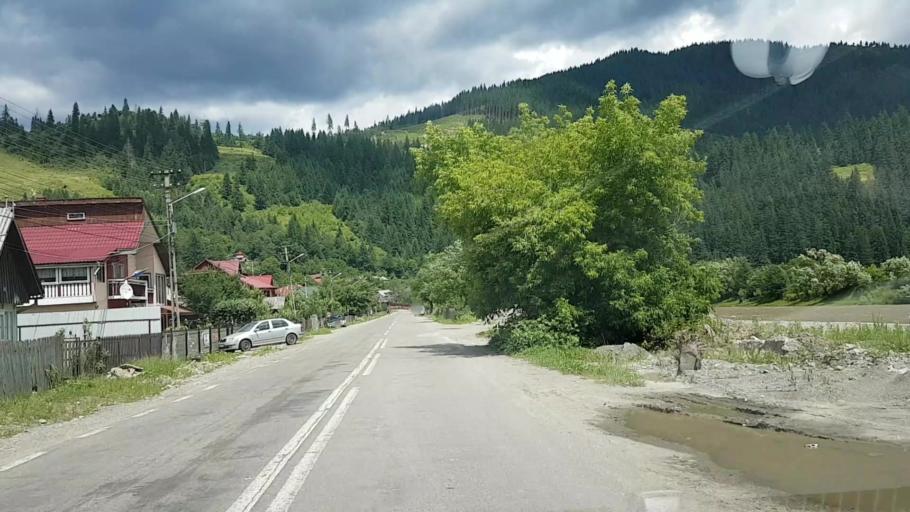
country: RO
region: Suceava
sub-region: Comuna Brosteni
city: Brosteni
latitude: 47.2403
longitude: 25.6999
